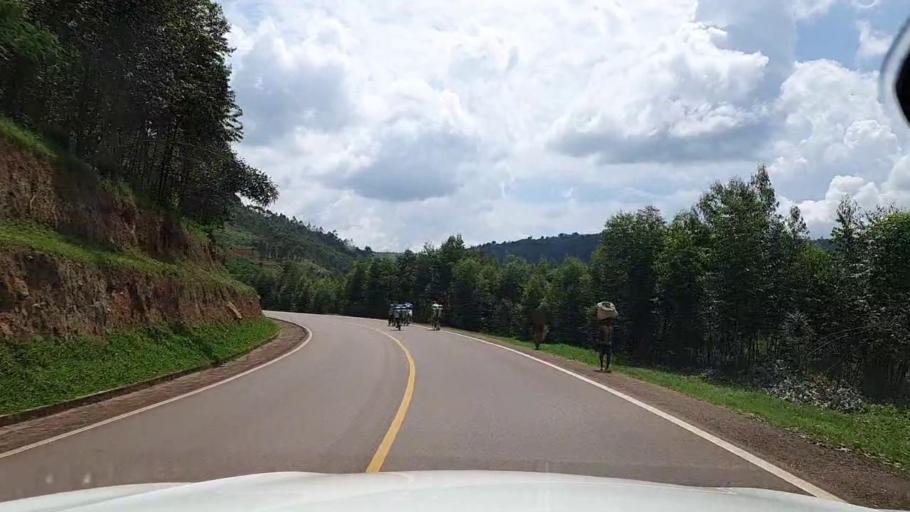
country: RW
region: Kigali
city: Kigali
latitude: -1.8145
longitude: 30.1065
